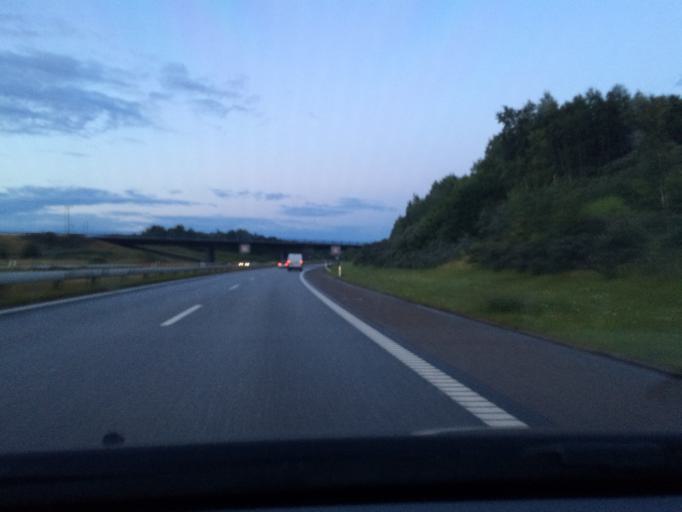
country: DK
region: Capital Region
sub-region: Frederiksberg Kommune
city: Frederiksberg
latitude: 55.6291
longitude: 12.5421
